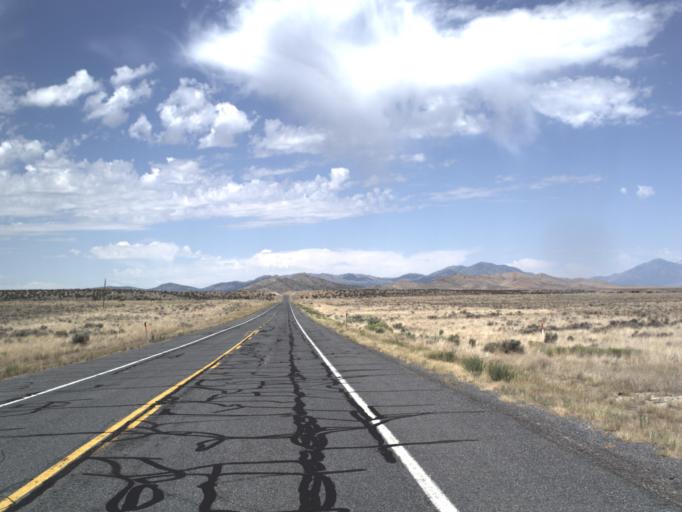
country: US
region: Utah
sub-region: Utah County
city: Eagle Mountain
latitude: 40.0543
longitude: -112.3005
